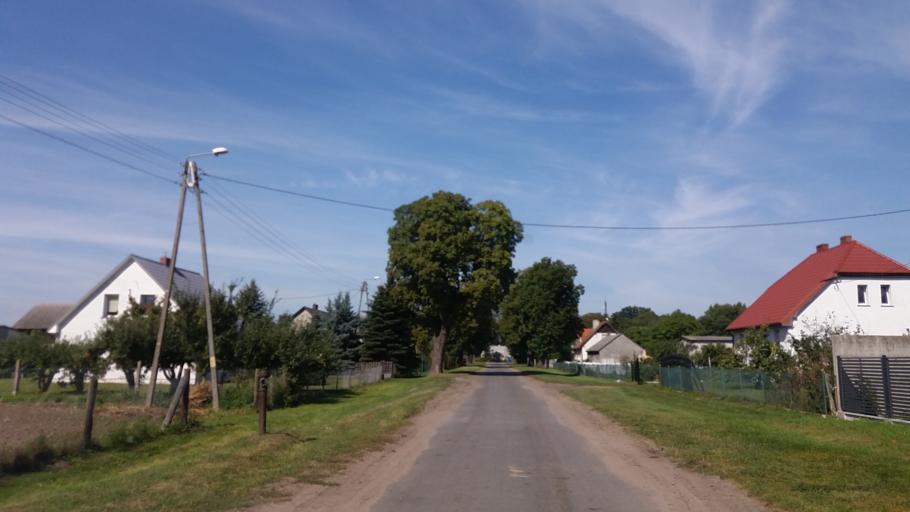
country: PL
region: West Pomeranian Voivodeship
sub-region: Powiat choszczenski
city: Choszczno
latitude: 53.1029
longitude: 15.4085
